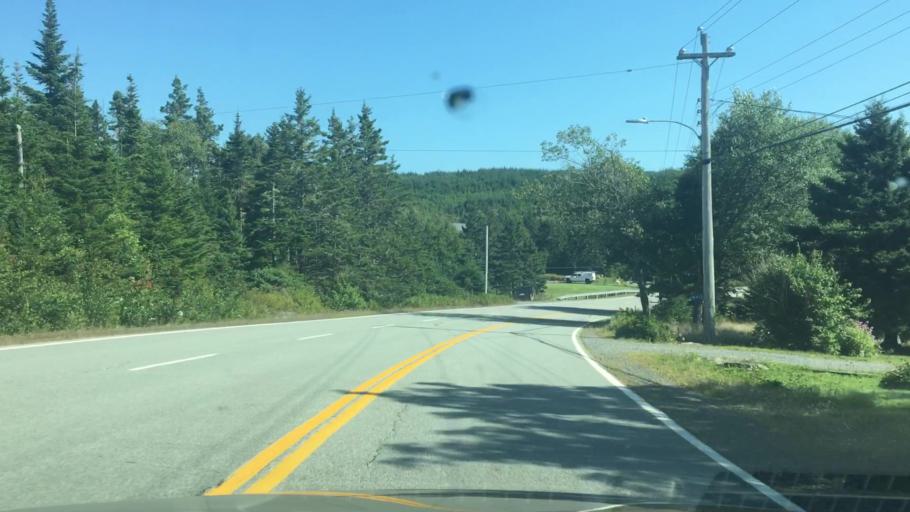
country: CA
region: Nova Scotia
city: New Glasgow
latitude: 44.8138
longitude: -62.6401
